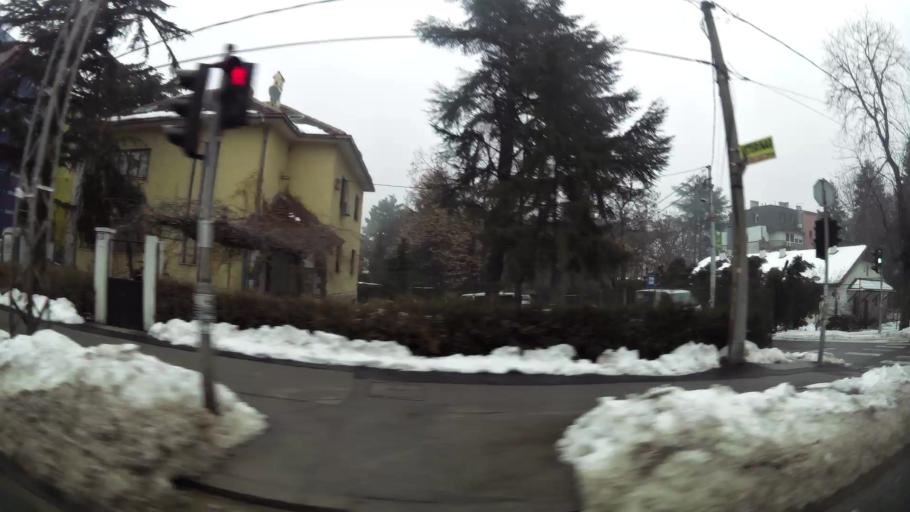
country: RS
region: Central Serbia
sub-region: Belgrade
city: Savski Venac
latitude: 44.7750
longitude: 20.4610
